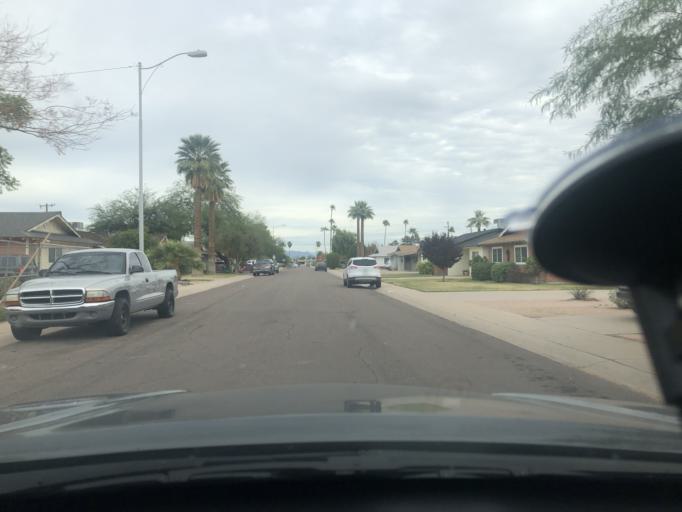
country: US
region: Arizona
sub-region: Maricopa County
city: Scottsdale
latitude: 33.4781
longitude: -111.8979
